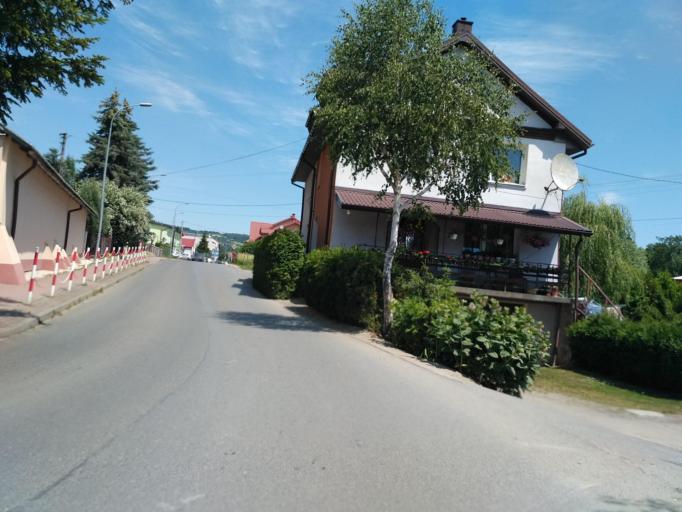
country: PL
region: Subcarpathian Voivodeship
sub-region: Powiat krosnienski
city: Korczyna
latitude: 49.7111
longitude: 21.8088
